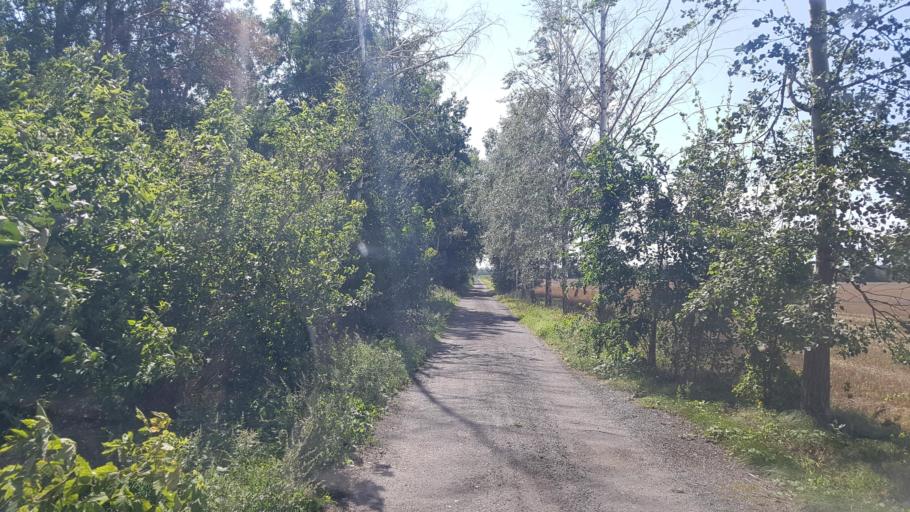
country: DE
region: Brandenburg
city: Bad Liebenwerda
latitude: 51.5144
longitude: 13.3384
